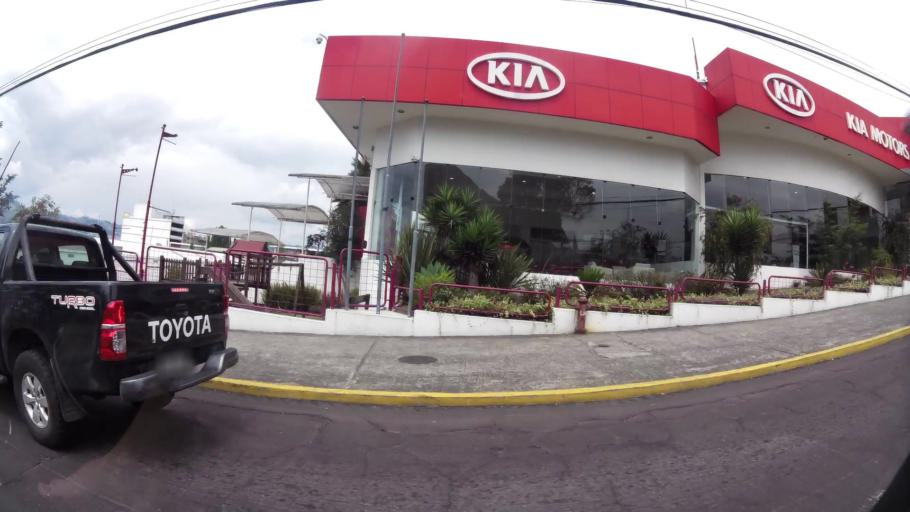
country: EC
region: Pichincha
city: Quito
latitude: -0.1863
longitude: -78.4966
